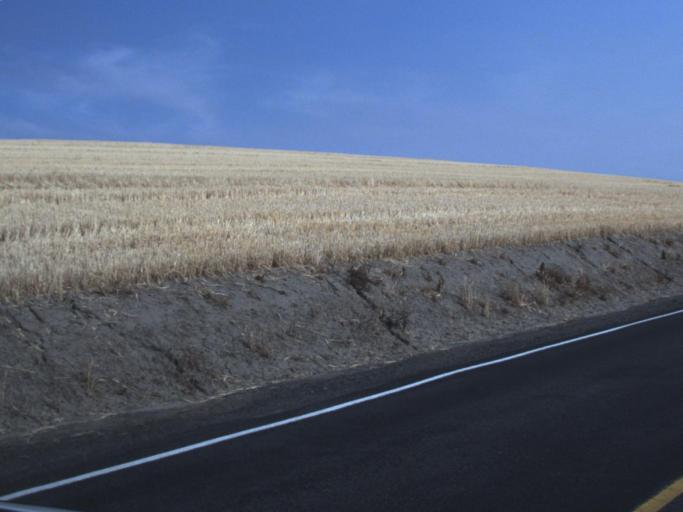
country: US
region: Idaho
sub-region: Benewah County
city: Plummer
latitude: 47.2352
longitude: -117.0504
